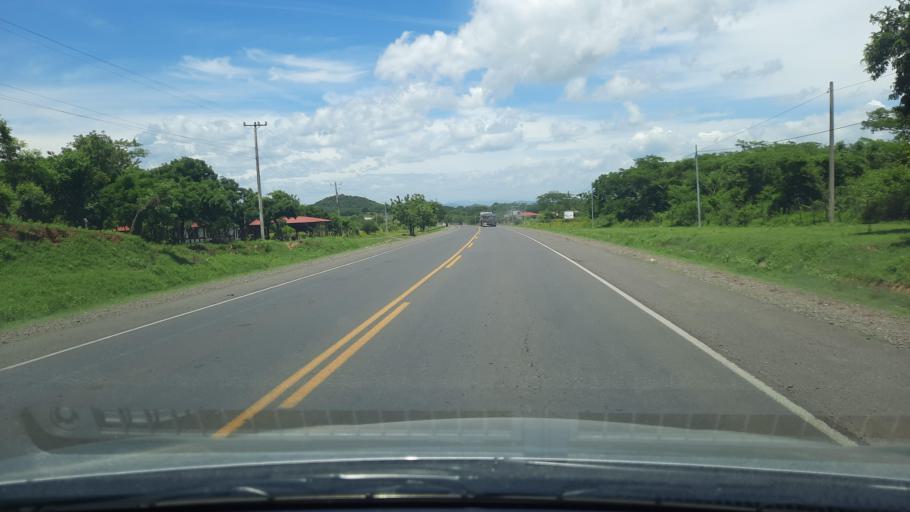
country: NI
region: Chinandega
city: Somotillo
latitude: 13.0566
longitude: -86.9230
